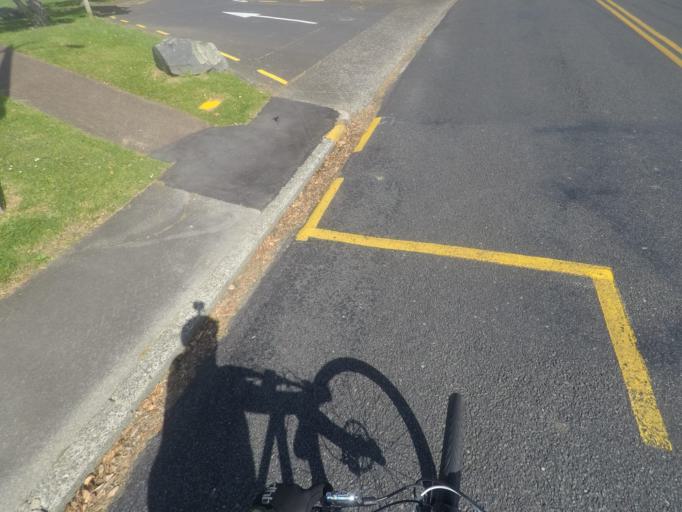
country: NZ
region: Auckland
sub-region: Auckland
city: Auckland
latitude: -36.9218
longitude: 174.7592
